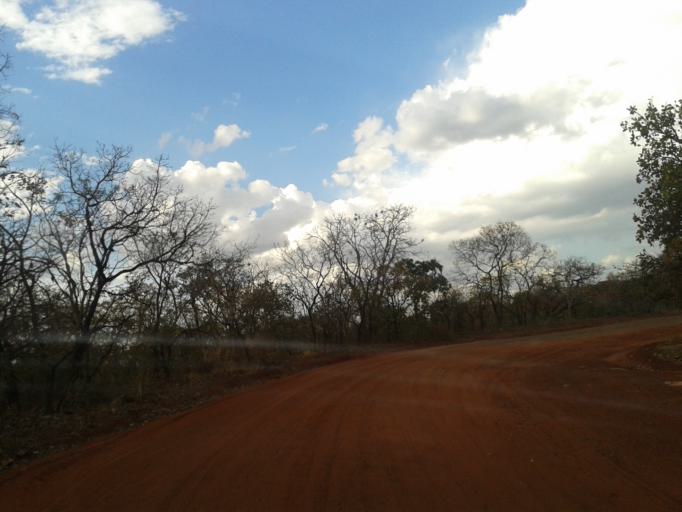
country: BR
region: Minas Gerais
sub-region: Santa Vitoria
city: Santa Vitoria
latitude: -19.1949
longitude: -49.8829
